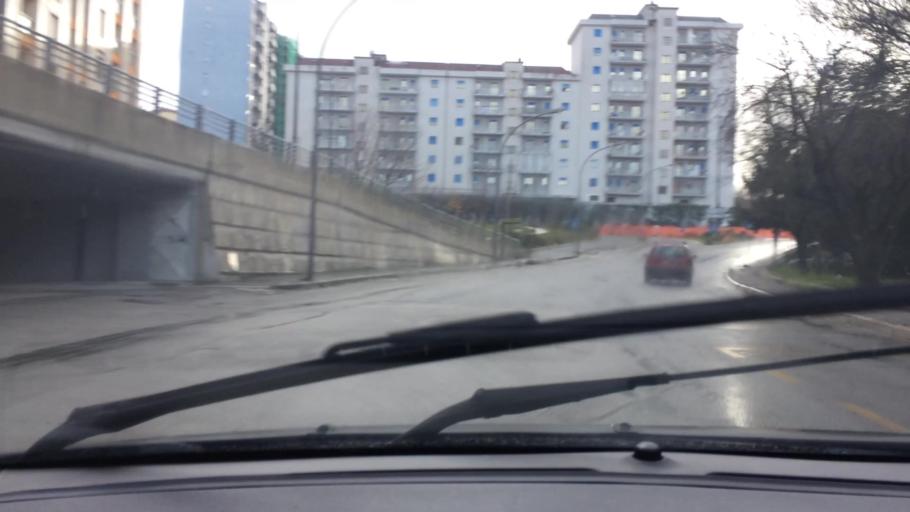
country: IT
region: Basilicate
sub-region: Provincia di Potenza
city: Potenza
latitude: 40.6415
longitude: 15.7895
